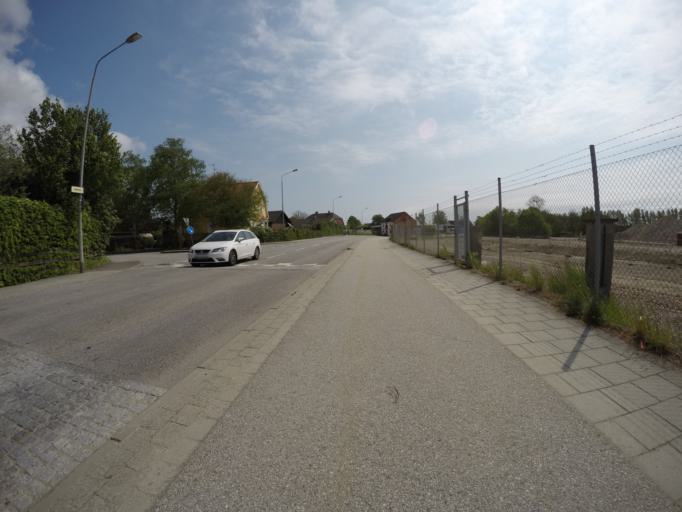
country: SE
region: Skane
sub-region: Malmo
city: Tygelsjo
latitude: 55.5152
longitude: 12.9975
